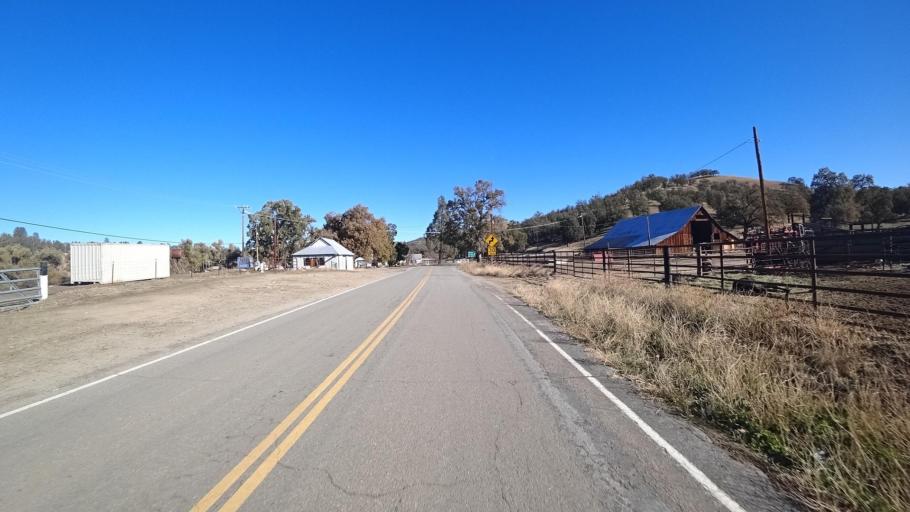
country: US
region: California
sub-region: Kern County
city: Alta Sierra
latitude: 35.7351
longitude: -118.7207
